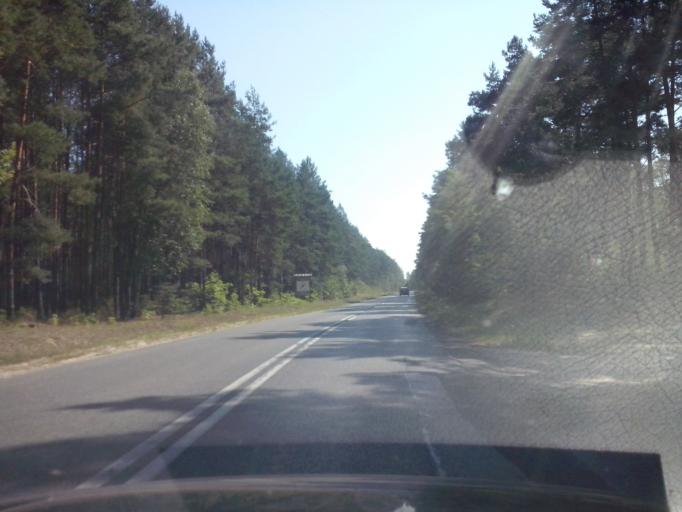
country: PL
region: Swietokrzyskie
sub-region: Powiat kielecki
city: Domaszowice
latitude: 50.8142
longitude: 20.7170
